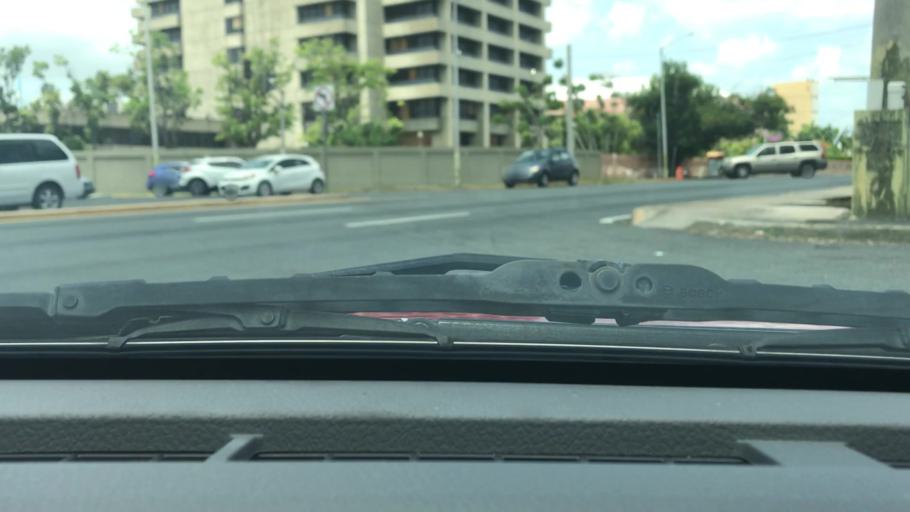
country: PR
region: Bayamon
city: Bayamon
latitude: 18.3958
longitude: -66.1484
